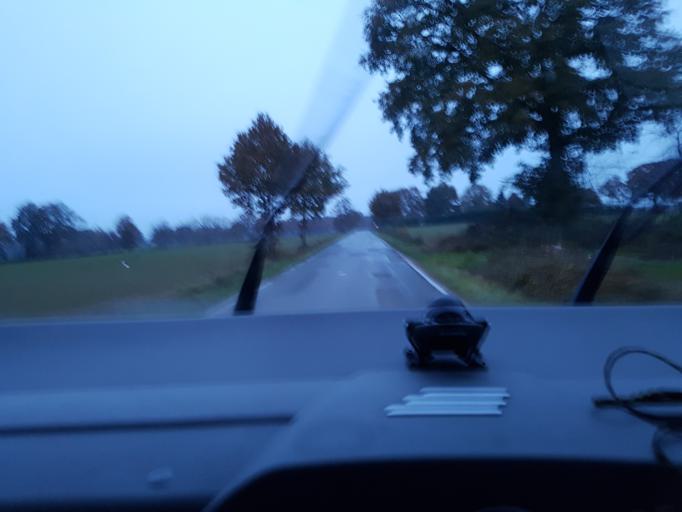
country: FR
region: Brittany
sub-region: Departement d'Ille-et-Vilaine
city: Montreuil-sous-Perouse
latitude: 48.2055
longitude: -1.2570
